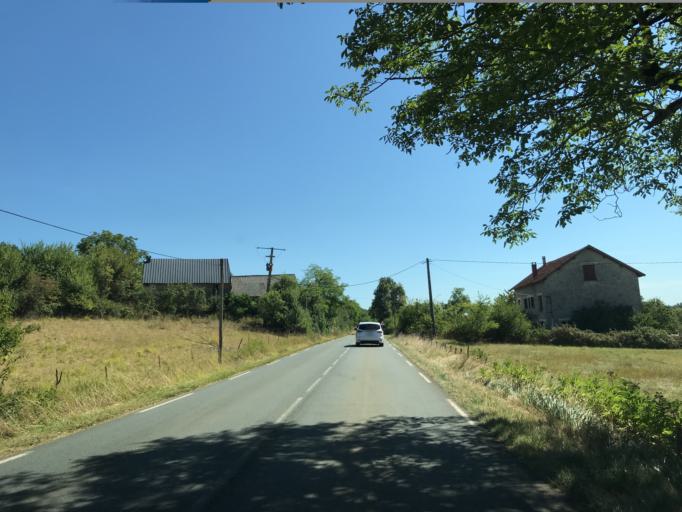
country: FR
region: Limousin
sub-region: Departement de la Correze
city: Larche
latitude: 45.0935
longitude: 1.3840
